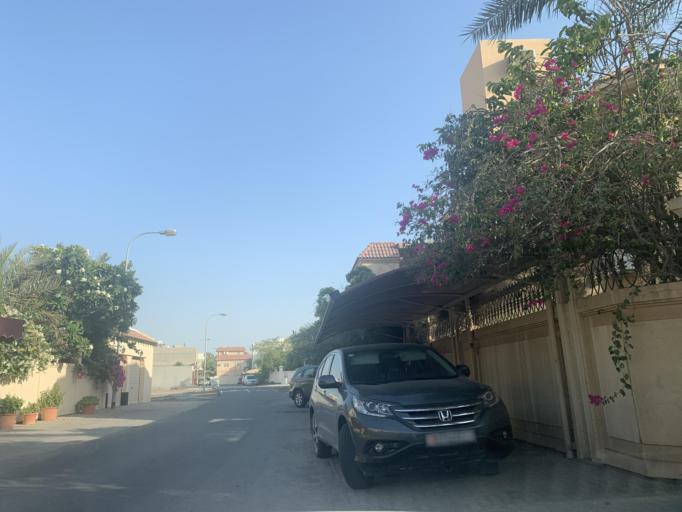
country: BH
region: Manama
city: Jidd Hafs
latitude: 26.2113
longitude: 50.5324
